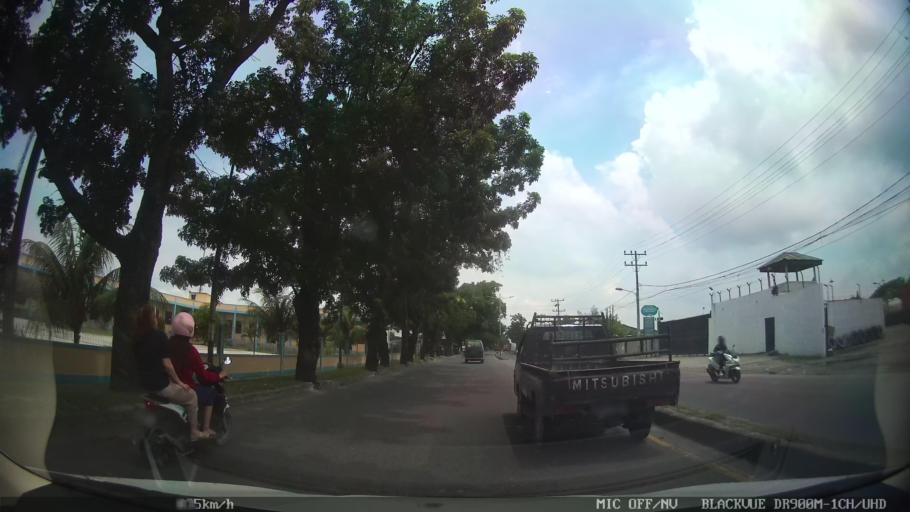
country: ID
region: North Sumatra
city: Labuhan Deli
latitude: 3.6778
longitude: 98.6652
